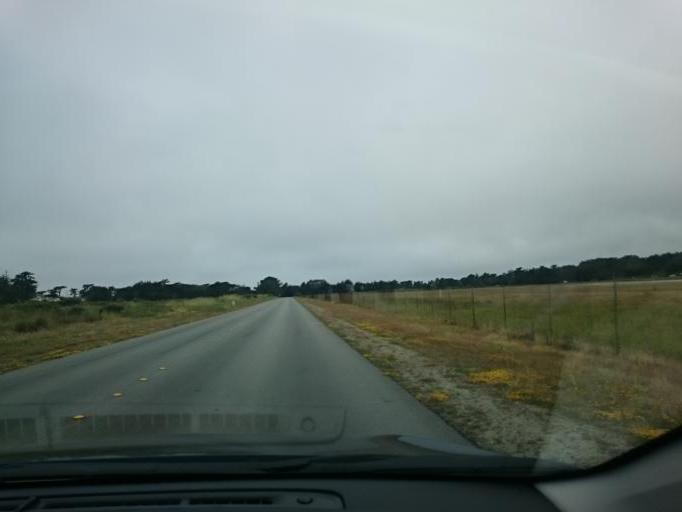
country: US
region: California
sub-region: San Mateo County
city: Moss Beach
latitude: 37.5167
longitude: -122.5065
